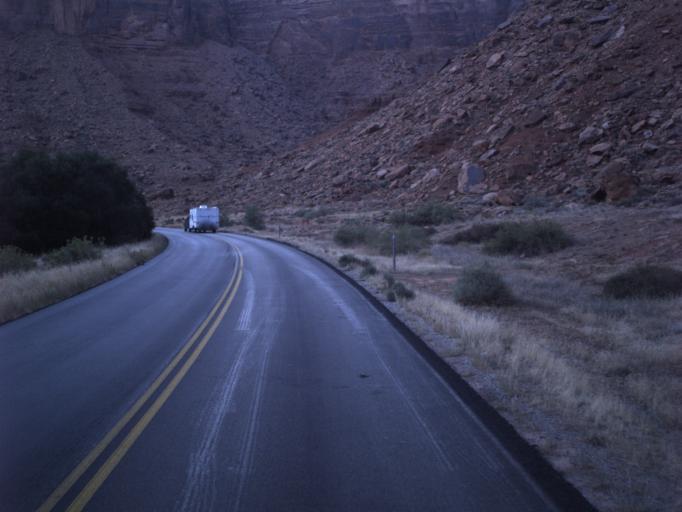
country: US
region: Utah
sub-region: Grand County
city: Moab
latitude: 38.6455
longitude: -109.4761
